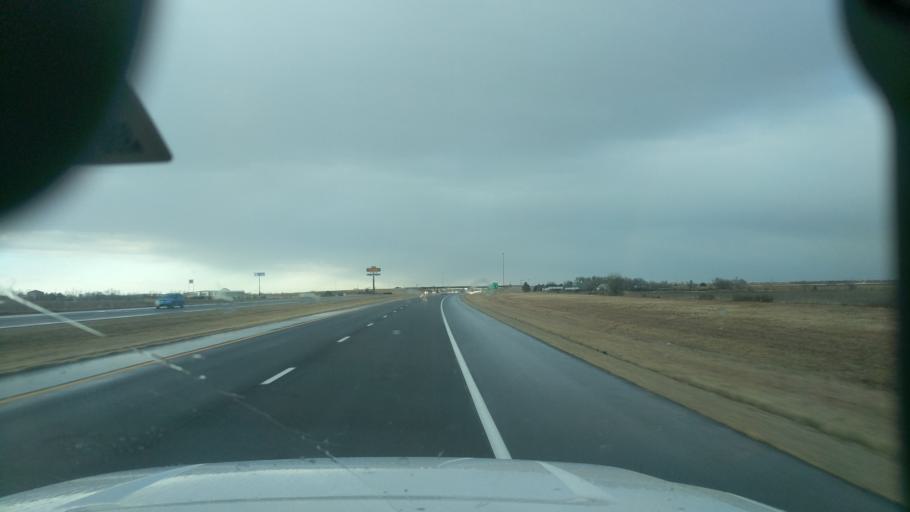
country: US
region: Kansas
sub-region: Harvey County
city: Newton
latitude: 37.9926
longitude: -97.3280
